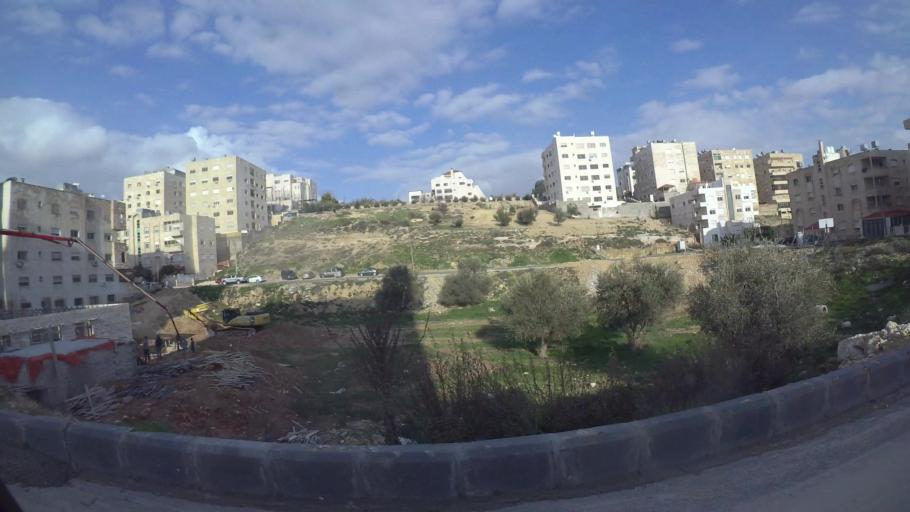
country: JO
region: Amman
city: Al Jubayhah
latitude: 32.0037
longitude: 35.8643
